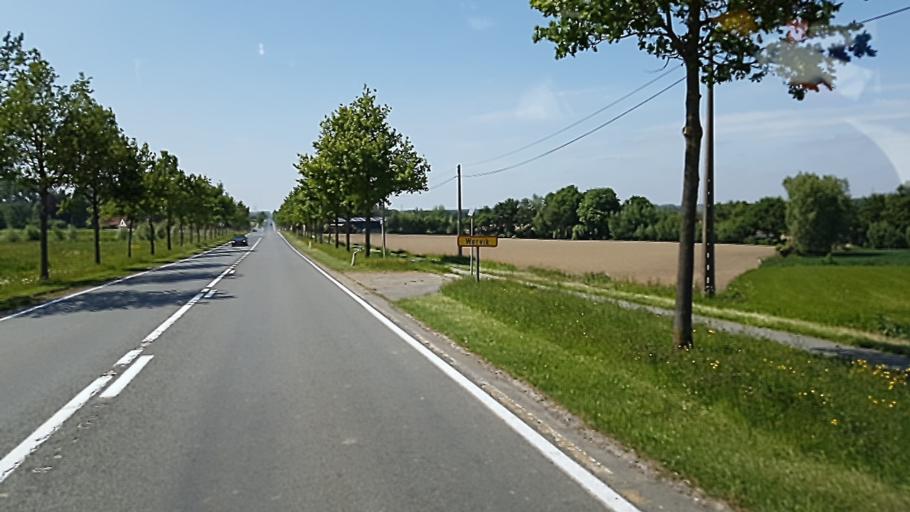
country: BE
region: Flanders
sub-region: Provincie West-Vlaanderen
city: Wervik
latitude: 50.8208
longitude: 3.0380
